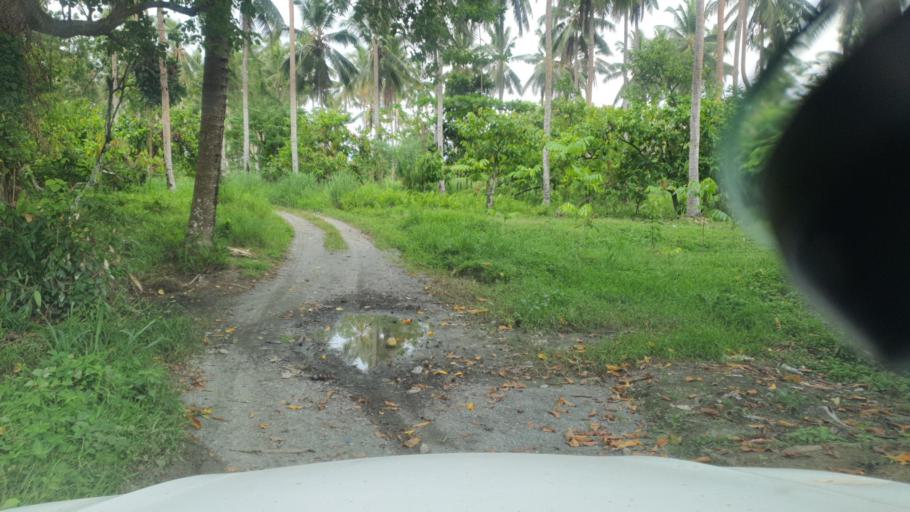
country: SB
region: Guadalcanal
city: Honiara
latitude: -9.4268
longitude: 160.2780
